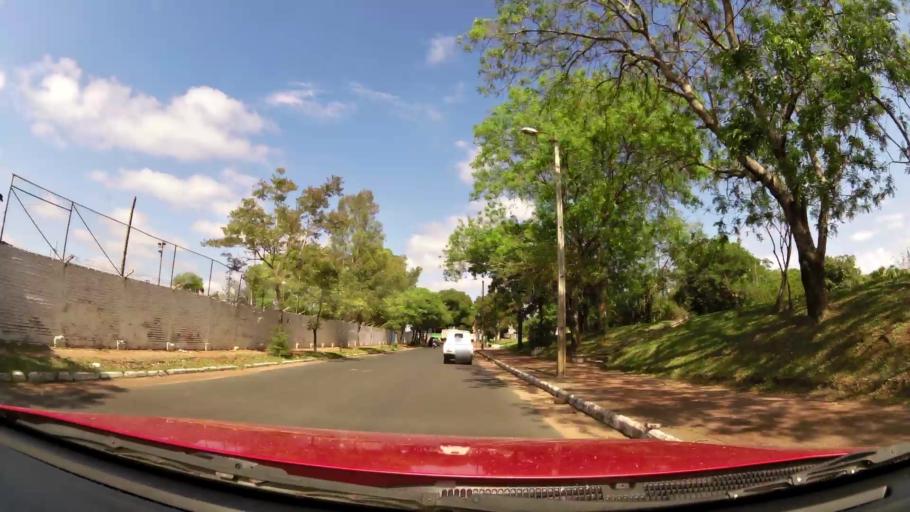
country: PY
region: Central
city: San Lorenzo
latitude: -25.2650
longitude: -57.4982
